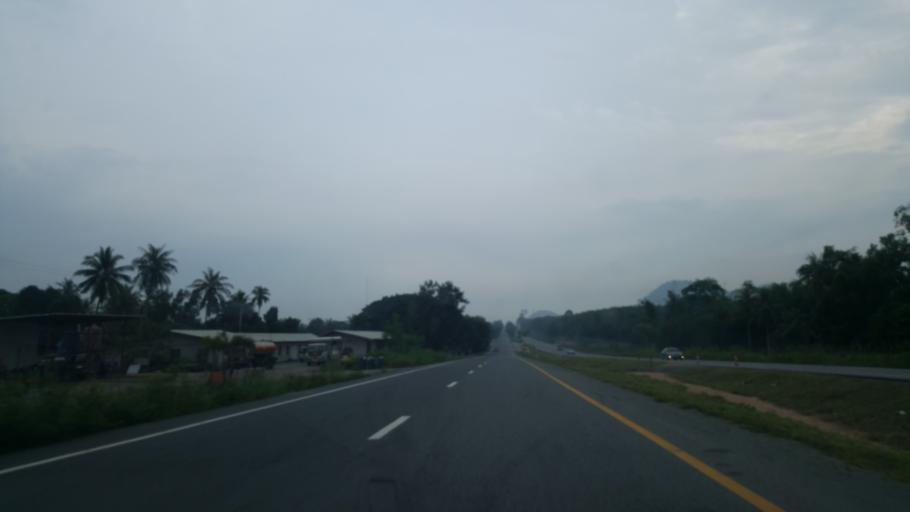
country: TH
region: Rayong
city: Ban Chang
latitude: 12.7963
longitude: 100.9921
